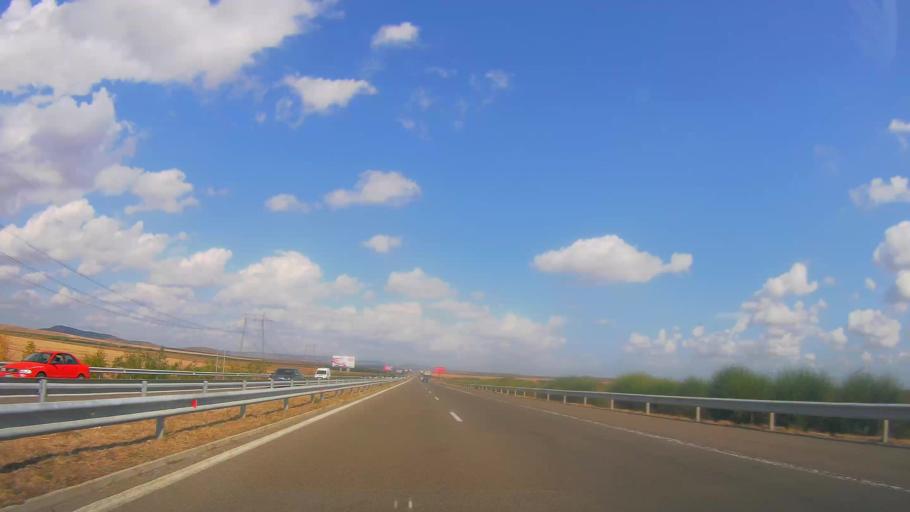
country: BG
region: Burgas
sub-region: Obshtina Kameno
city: Kameno
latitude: 42.5898
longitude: 27.2285
